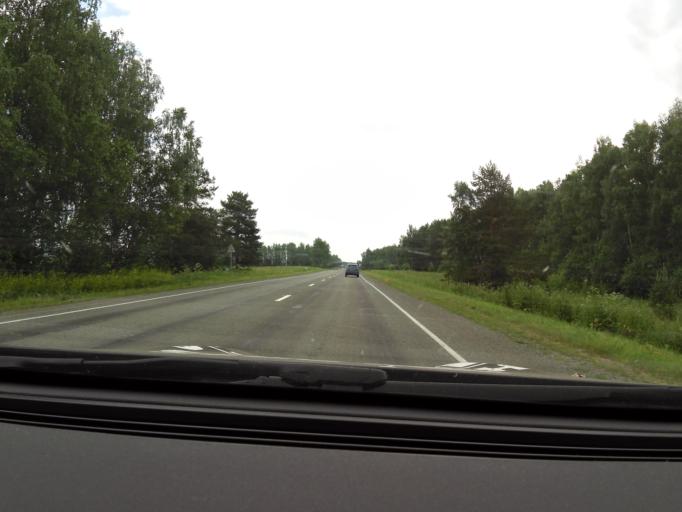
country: RU
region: Perm
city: Suksun
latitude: 56.9176
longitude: 57.5753
